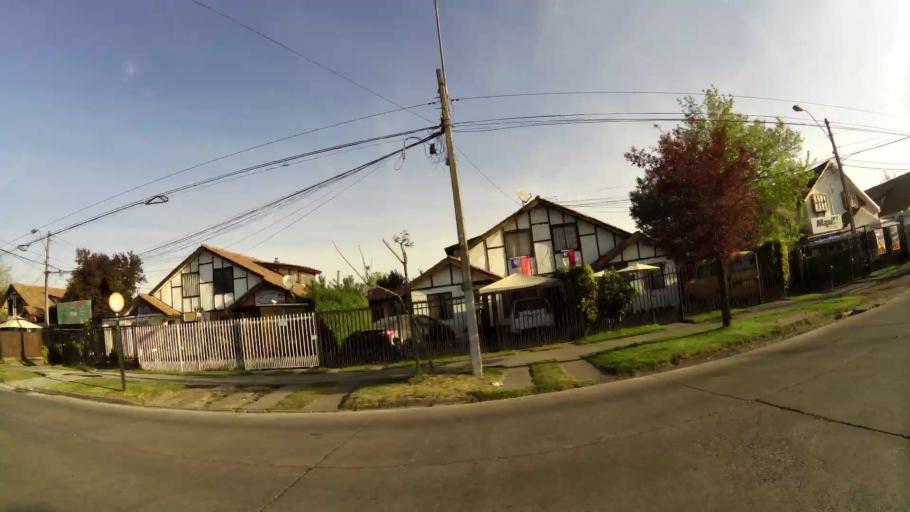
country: CL
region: Santiago Metropolitan
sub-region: Provincia de Cordillera
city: Puente Alto
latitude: -33.5437
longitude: -70.5755
